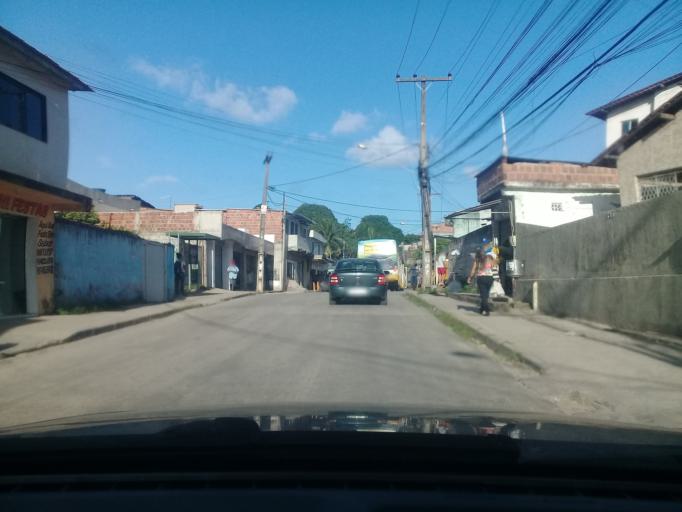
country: BR
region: Pernambuco
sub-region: Jaboatao Dos Guararapes
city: Jaboatao dos Guararapes
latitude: -8.1029
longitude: -34.9663
